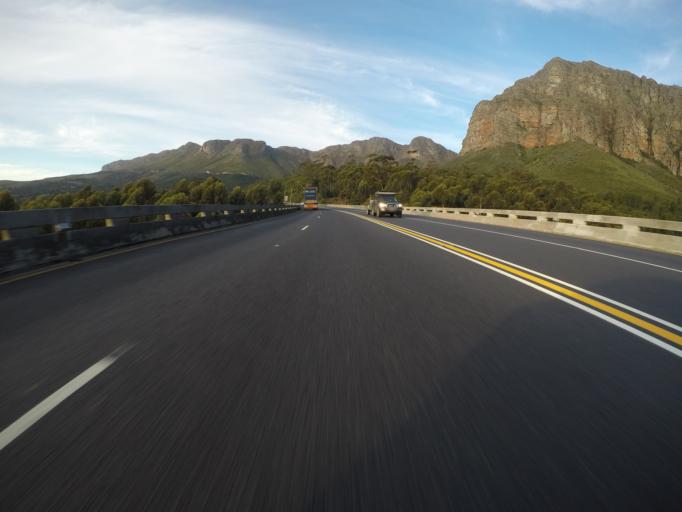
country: ZA
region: Western Cape
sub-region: Cape Winelands District Municipality
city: Paarl
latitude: -33.7446
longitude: 19.0635
